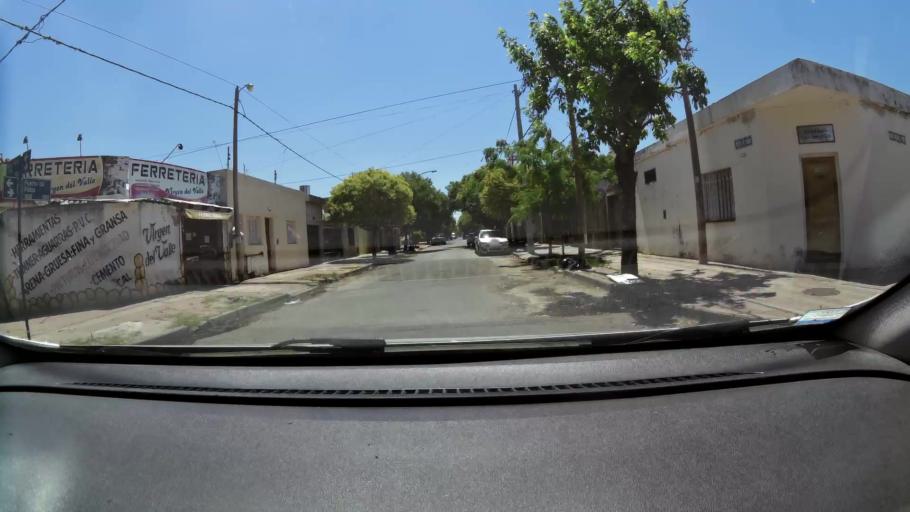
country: AR
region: Cordoba
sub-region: Departamento de Capital
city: Cordoba
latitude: -31.3889
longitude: -64.1558
